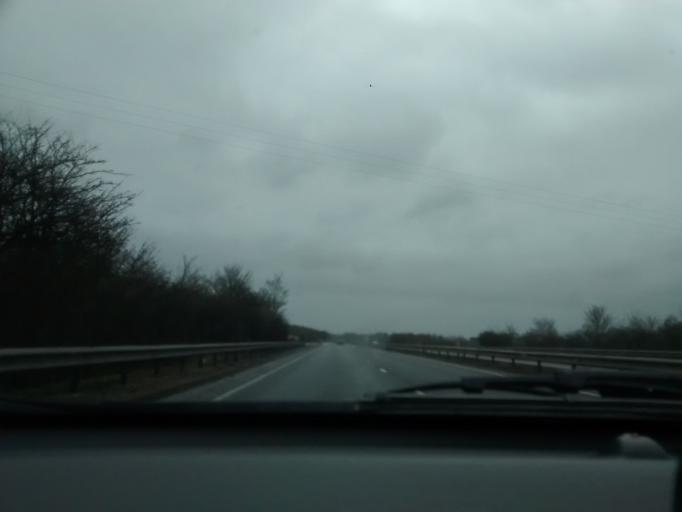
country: GB
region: England
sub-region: Suffolk
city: Stowmarket
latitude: 52.1856
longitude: 1.0257
